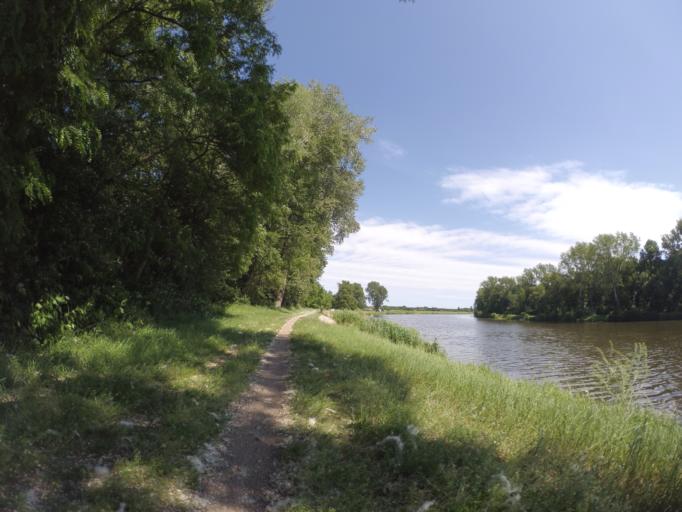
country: CZ
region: Central Bohemia
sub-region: Okres Nymburk
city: Sadska
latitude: 50.1685
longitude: 14.9483
